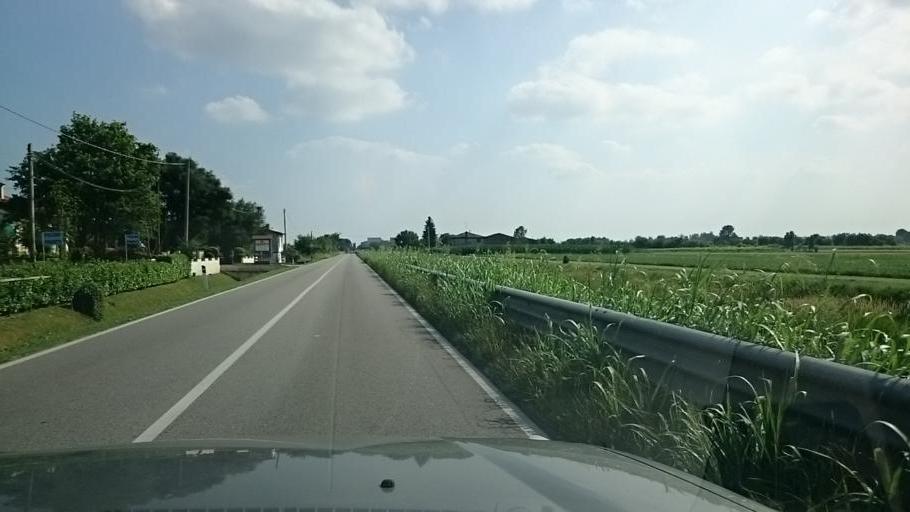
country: IT
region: Veneto
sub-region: Provincia di Padova
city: Cavino
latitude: 45.5285
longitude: 11.8698
